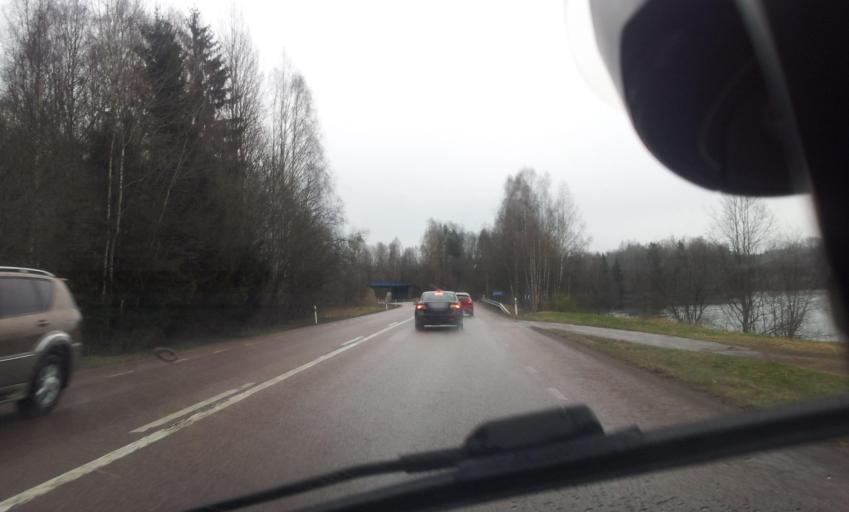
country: SE
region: Dalarna
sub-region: Gagnefs Kommun
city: Djuras
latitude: 60.5430
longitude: 15.2798
